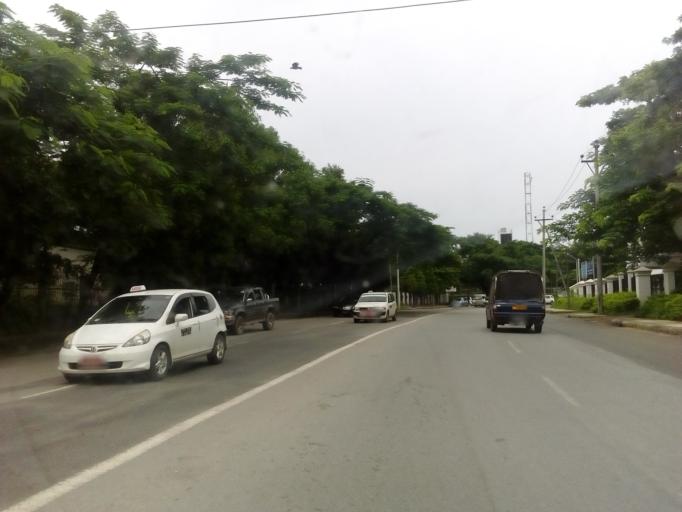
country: MM
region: Yangon
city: Yangon
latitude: 16.8538
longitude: 96.1374
